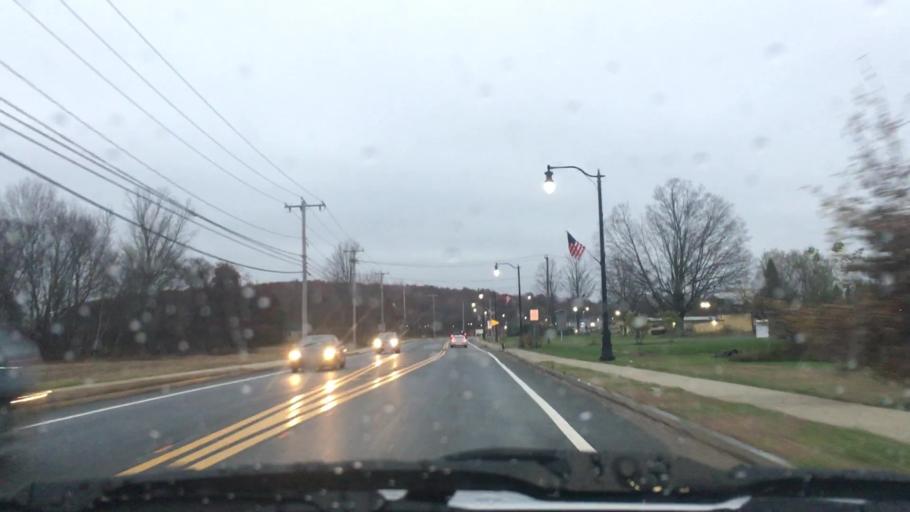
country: US
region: Massachusetts
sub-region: Hampden County
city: Southwick
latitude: 42.0720
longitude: -72.7655
